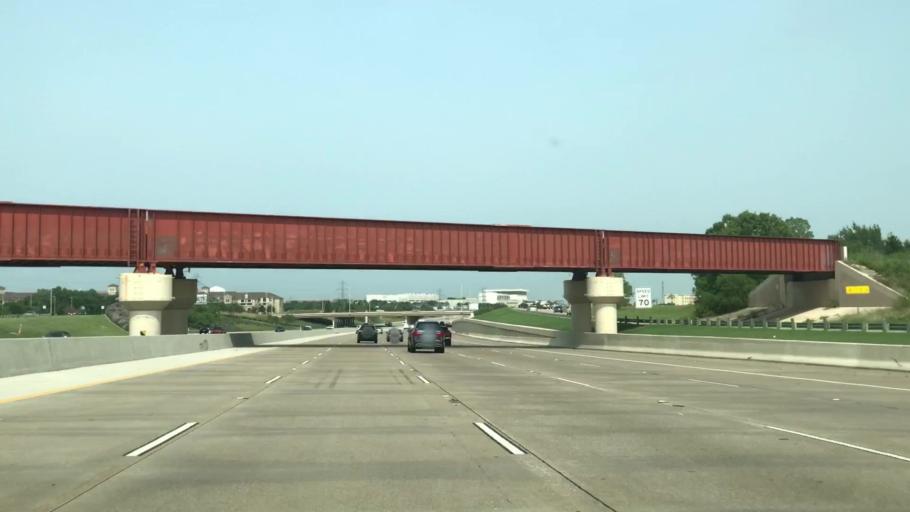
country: US
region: Texas
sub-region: Collin County
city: Plano
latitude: 33.0017
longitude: -96.7526
